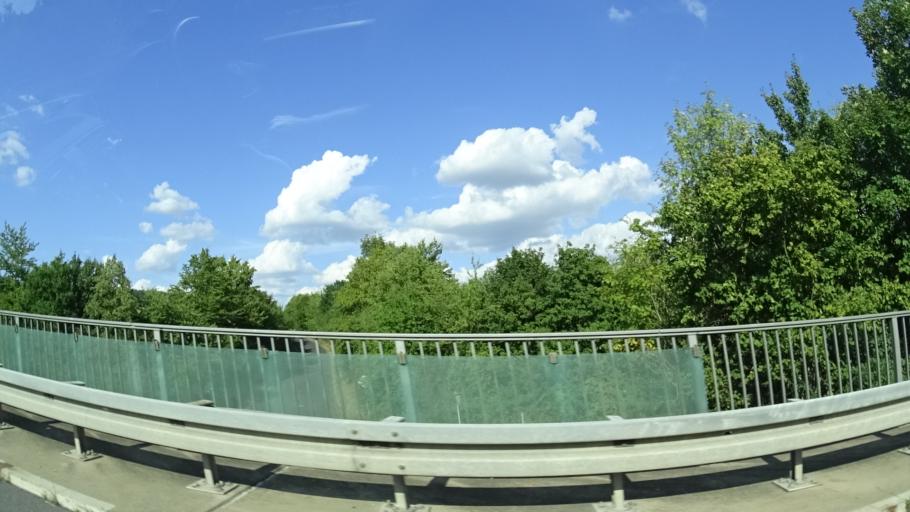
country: DE
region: Bavaria
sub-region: Regierungsbezirk Unterfranken
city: Oberelsbach
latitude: 50.3814
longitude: 10.1104
